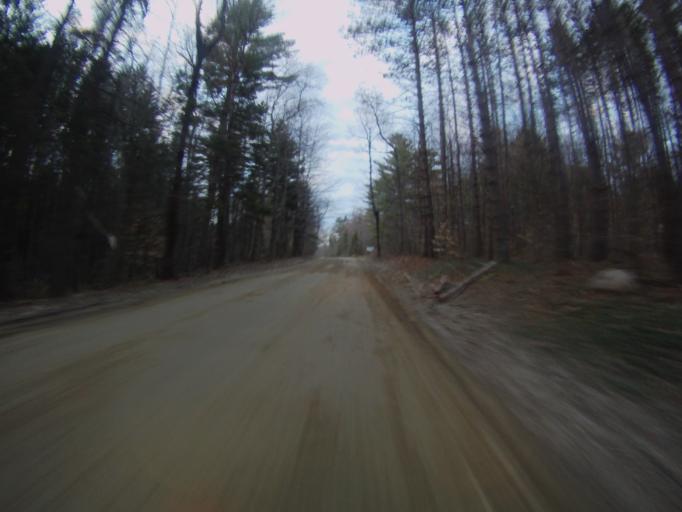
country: US
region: Vermont
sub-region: Addison County
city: Middlebury (village)
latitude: 43.9564
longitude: -73.0259
